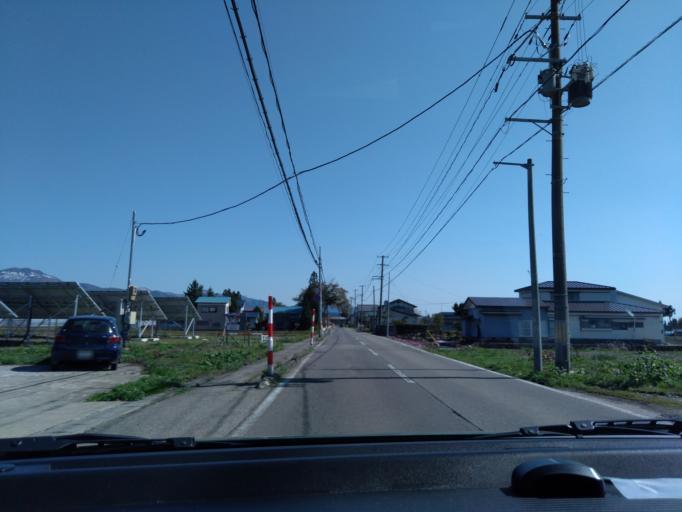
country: JP
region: Akita
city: Kakunodatemachi
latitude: 39.5198
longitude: 140.5887
